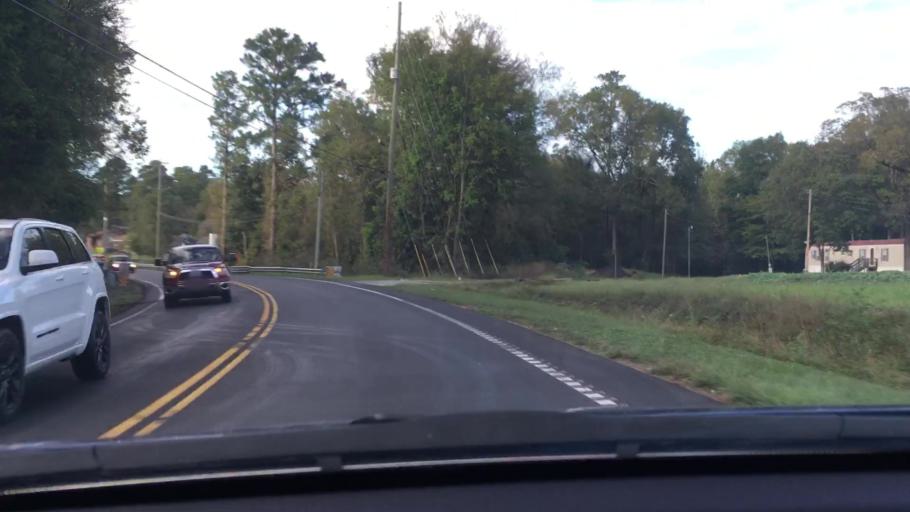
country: US
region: South Carolina
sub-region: Lexington County
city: Irmo
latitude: 34.1107
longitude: -81.1611
